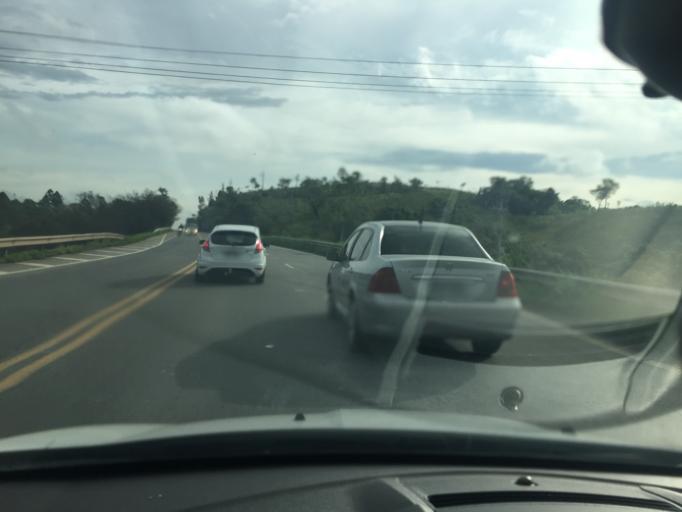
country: BR
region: Sao Paulo
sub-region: Campo Limpo Paulista
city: Campo Limpo Paulista
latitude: -23.1908
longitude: -46.7850
